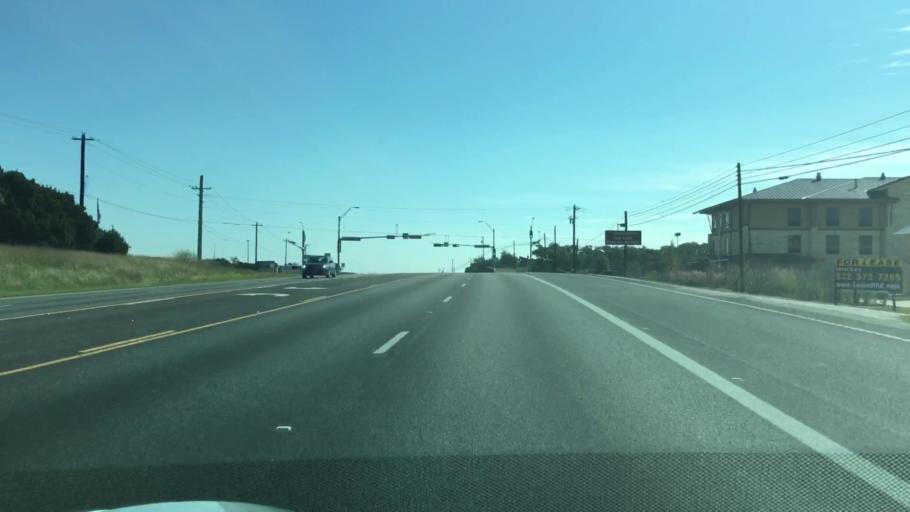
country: US
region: Texas
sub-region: Hays County
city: Dripping Springs
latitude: 30.1940
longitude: -98.0450
